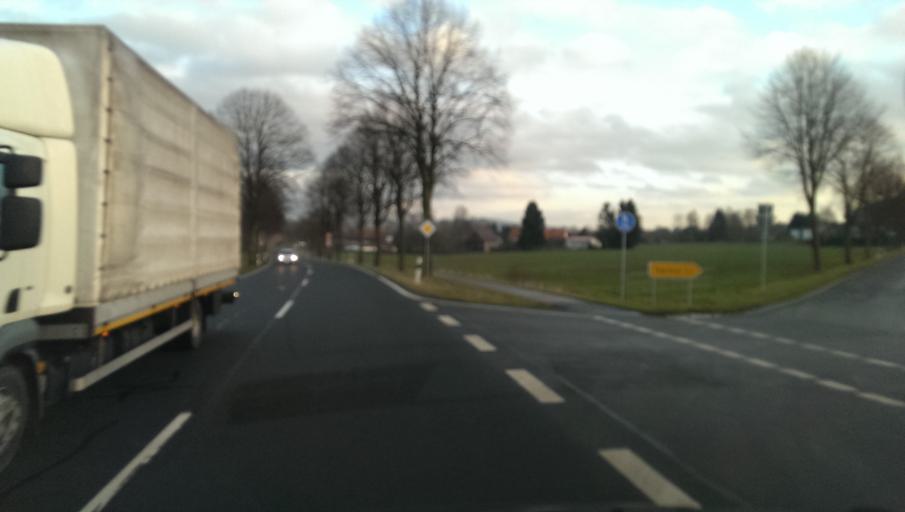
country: DE
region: Lower Saxony
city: Eimen
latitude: 51.8802
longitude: 9.7746
